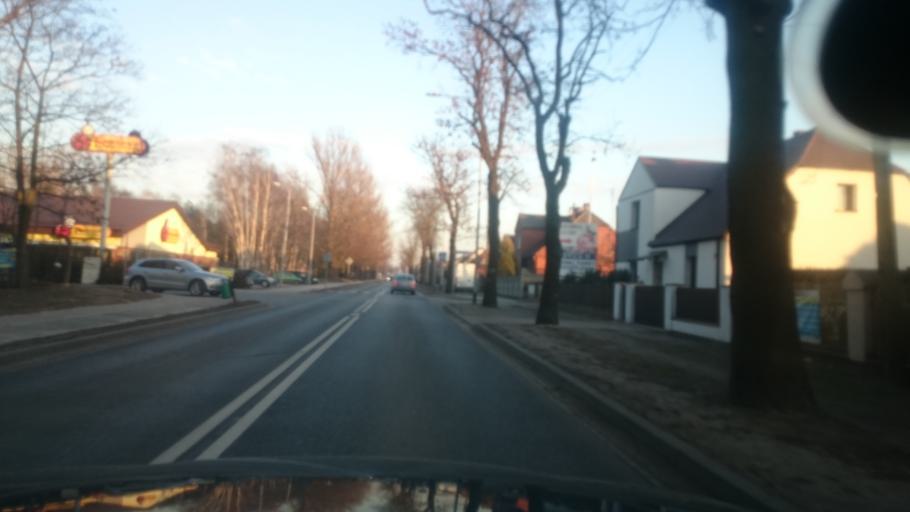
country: PL
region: Greater Poland Voivodeship
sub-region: Powiat ostrowski
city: Ostrow Wielkopolski
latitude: 51.6461
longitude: 17.8553
